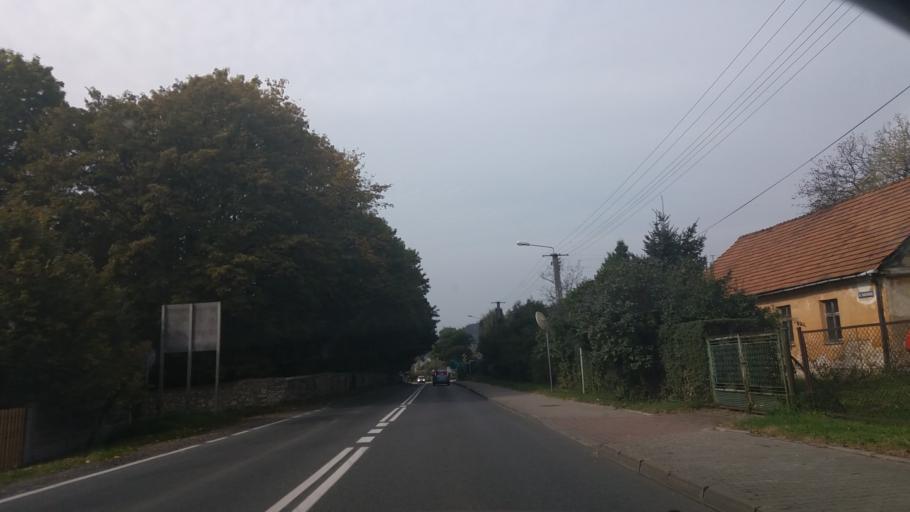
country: PL
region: Lesser Poland Voivodeship
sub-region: Powiat chrzanowski
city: Babice
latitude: 50.0738
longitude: 19.4393
